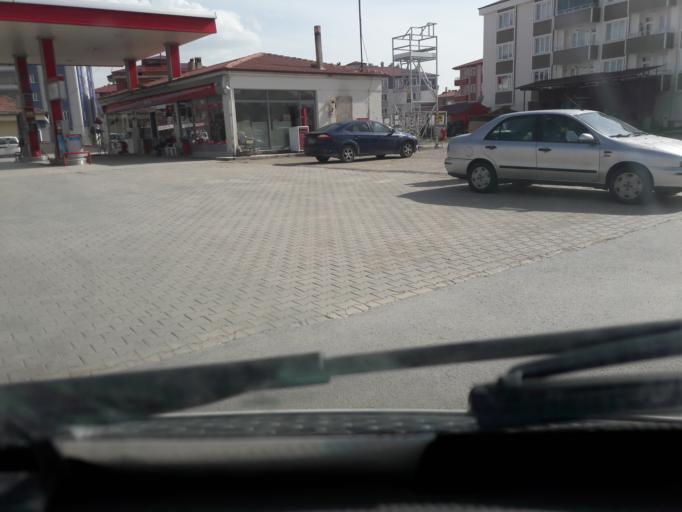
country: TR
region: Gumushane
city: Kelkit
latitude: 40.1341
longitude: 39.4353
